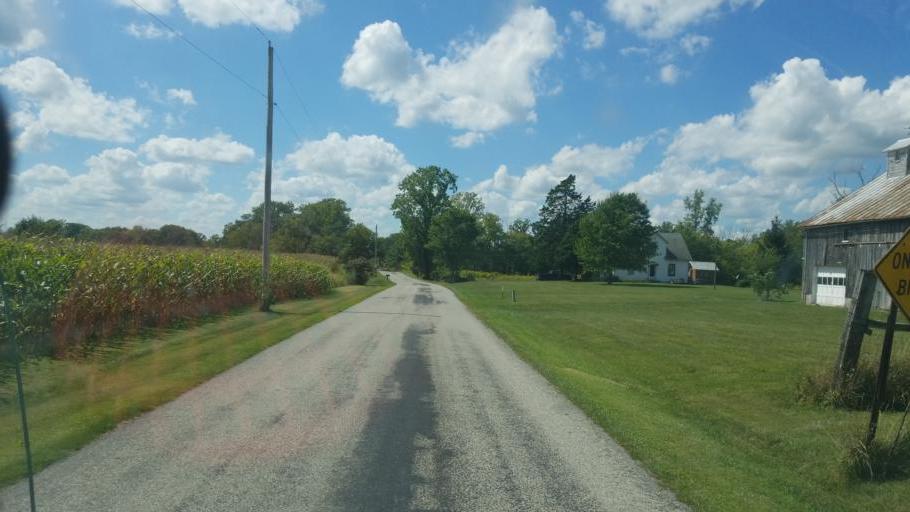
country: US
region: Ohio
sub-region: Marion County
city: Prospect
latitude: 40.3727
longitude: -83.2047
